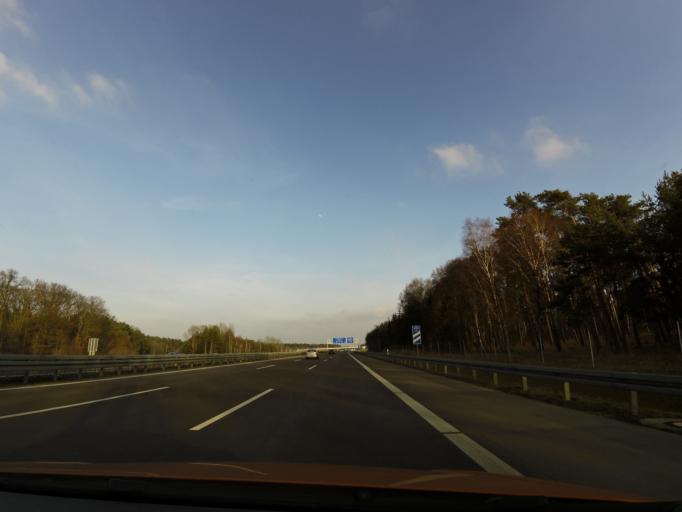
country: DE
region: Brandenburg
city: Kremmen
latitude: 52.7150
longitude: 12.9978
